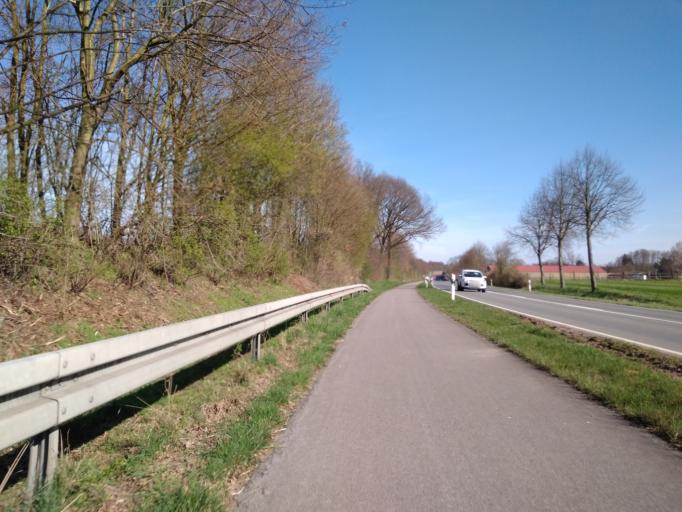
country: DE
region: North Rhine-Westphalia
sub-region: Regierungsbezirk Dusseldorf
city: Schermbeck
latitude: 51.6703
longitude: 6.8667
